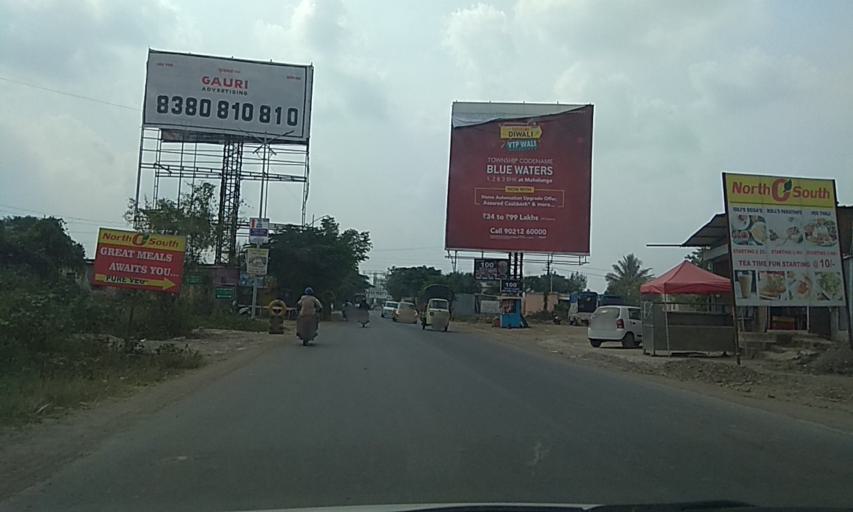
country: IN
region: Maharashtra
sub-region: Pune Division
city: Pimpri
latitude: 18.5794
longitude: 73.7183
